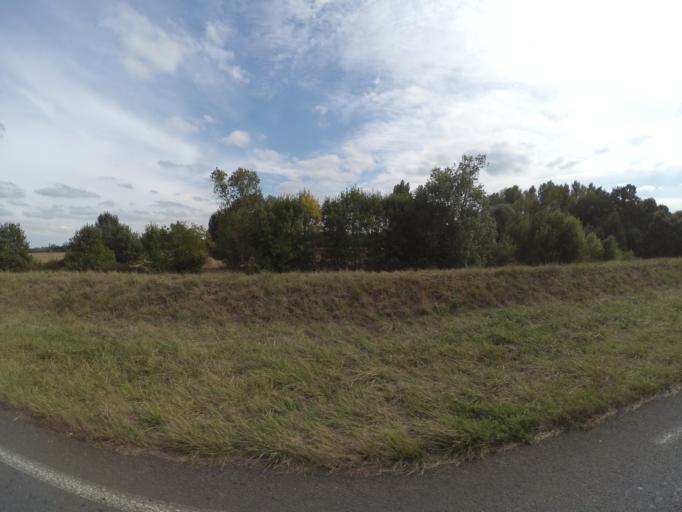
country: FR
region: Centre
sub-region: Departement d'Indre-et-Loire
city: Langeais
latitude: 47.3028
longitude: 0.3523
